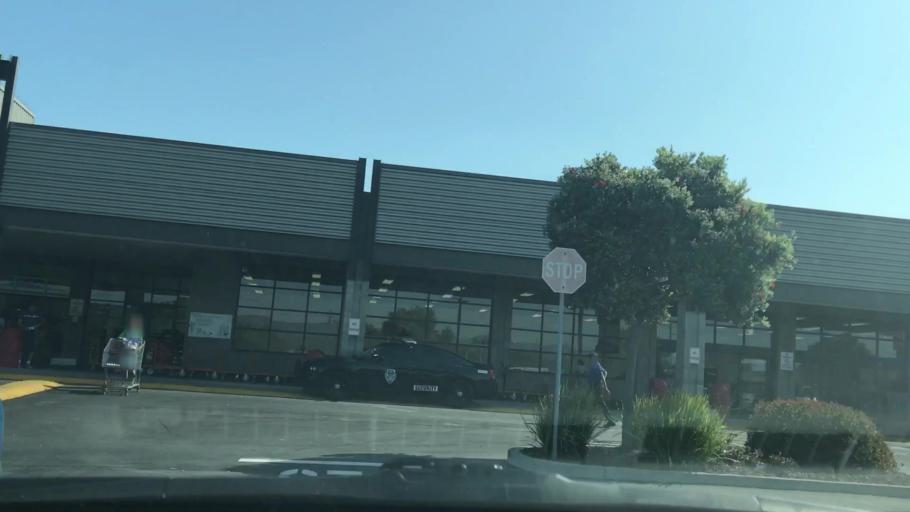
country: US
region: California
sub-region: San Mateo County
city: South San Francisco
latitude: 37.6418
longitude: -122.4015
